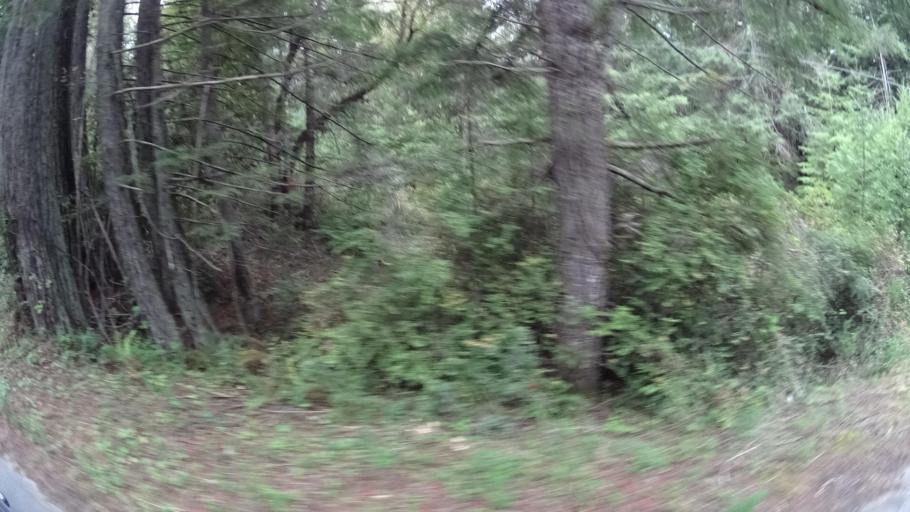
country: US
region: California
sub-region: Humboldt County
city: Redway
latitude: 40.2813
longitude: -123.7974
